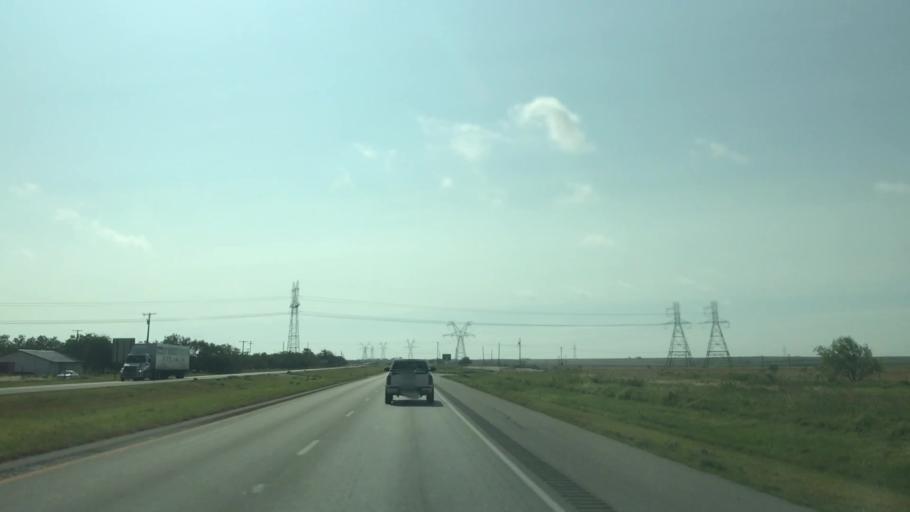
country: US
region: Texas
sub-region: Scurry County
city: Snyder
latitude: 32.6844
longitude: -100.8381
